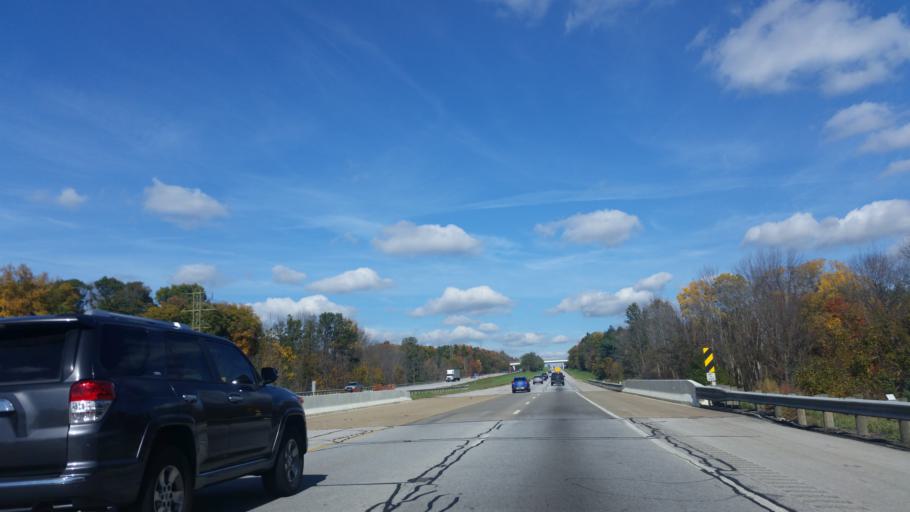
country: US
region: Ohio
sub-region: Summit County
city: Montrose-Ghent
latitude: 41.1684
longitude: -81.6259
